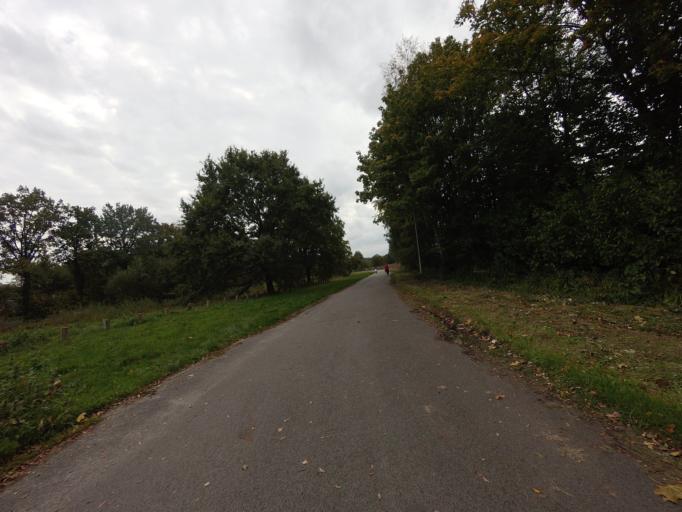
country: NL
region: North Brabant
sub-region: Gemeente Breda
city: Breda
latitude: 51.5605
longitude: 4.8018
